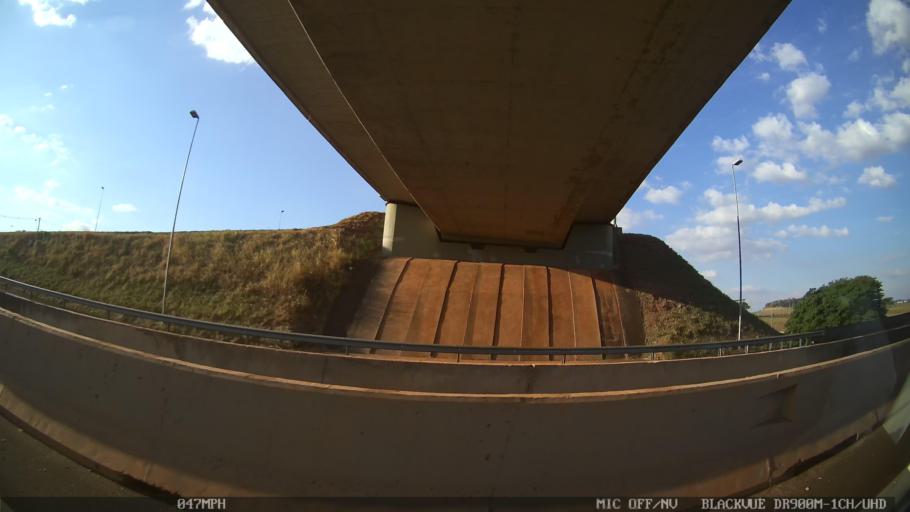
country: BR
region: Sao Paulo
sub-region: Ribeirao Preto
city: Ribeirao Preto
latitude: -21.2050
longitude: -47.7601
